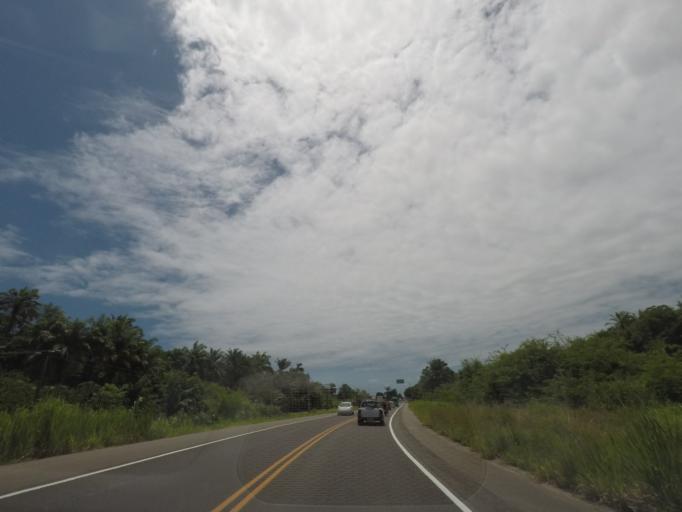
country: BR
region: Bahia
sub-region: Itaparica
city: Itaparica
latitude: -12.9839
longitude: -38.6319
